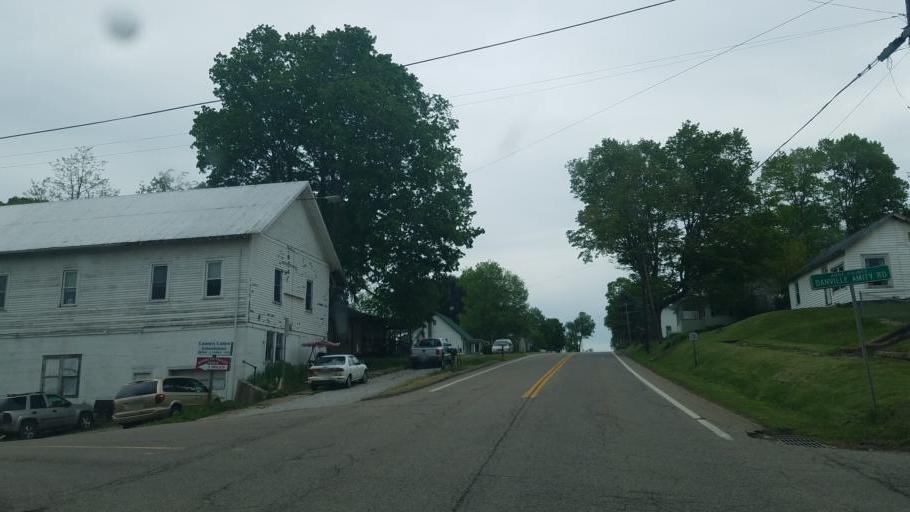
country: US
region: Ohio
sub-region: Knox County
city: Gambier
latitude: 40.4711
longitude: -82.3788
